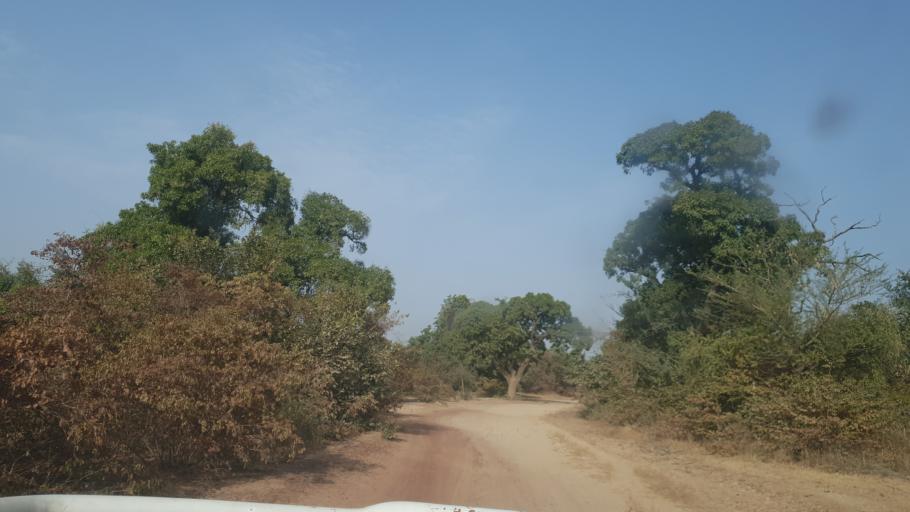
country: ML
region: Segou
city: Baroueli
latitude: 13.3720
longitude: -6.9146
